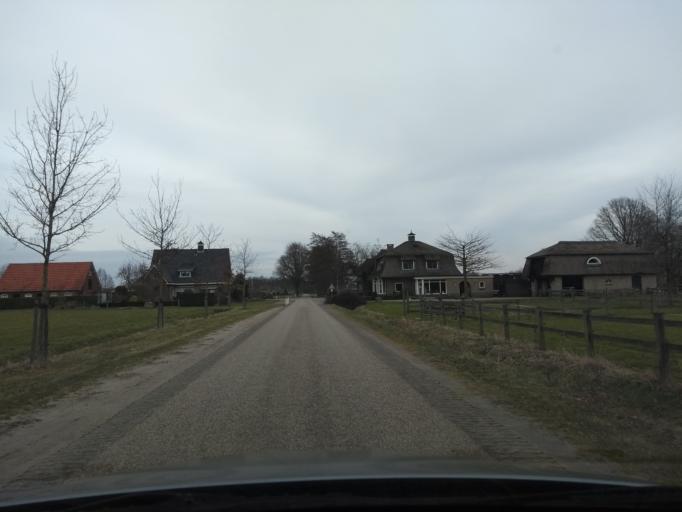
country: NL
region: Overijssel
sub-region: Gemeente Almelo
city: Almelo
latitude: 52.3675
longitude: 6.7214
